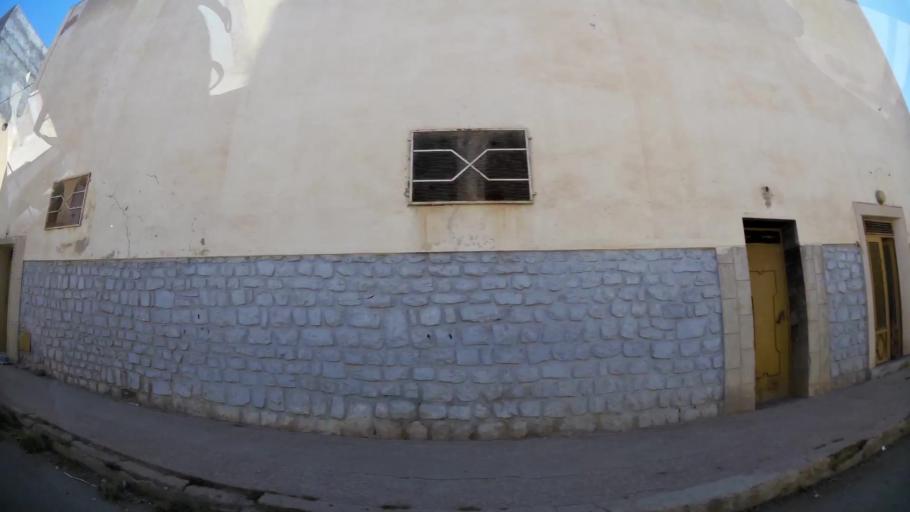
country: MA
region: Oriental
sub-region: Oujda-Angad
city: Oujda
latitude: 34.6661
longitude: -1.9352
